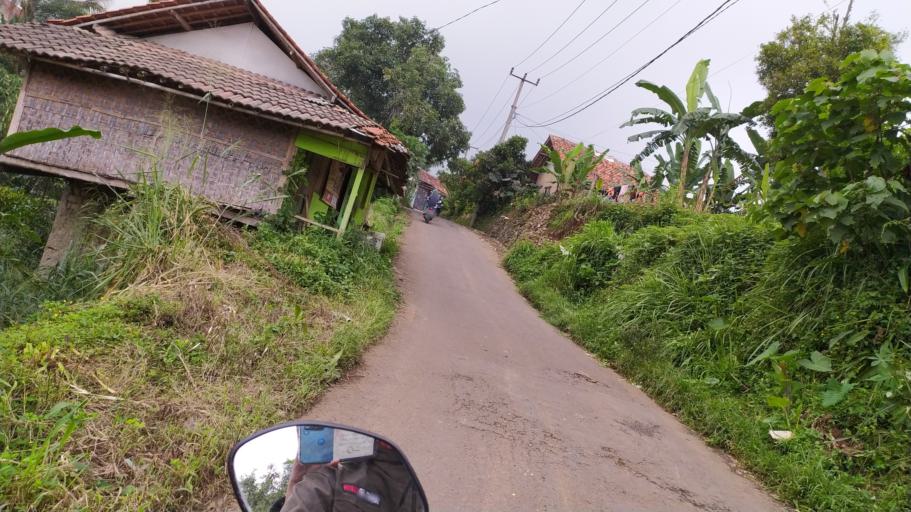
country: ID
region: West Java
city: Ciampea
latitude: -6.6463
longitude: 106.7048
